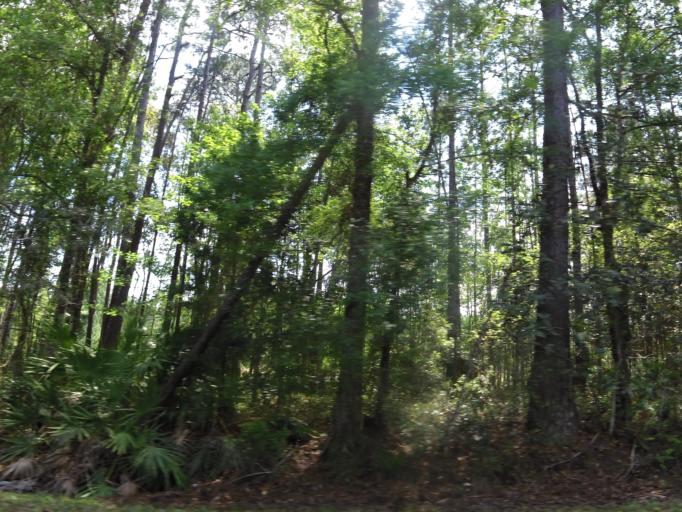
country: US
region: Florida
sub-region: Nassau County
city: Yulee
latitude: 30.5207
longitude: -81.6673
